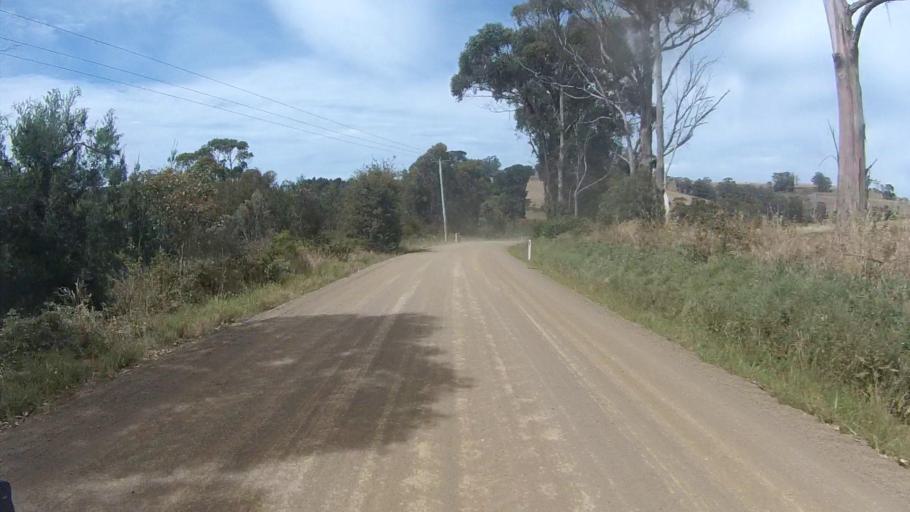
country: AU
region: Tasmania
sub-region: Sorell
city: Sorell
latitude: -42.8188
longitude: 147.8239
